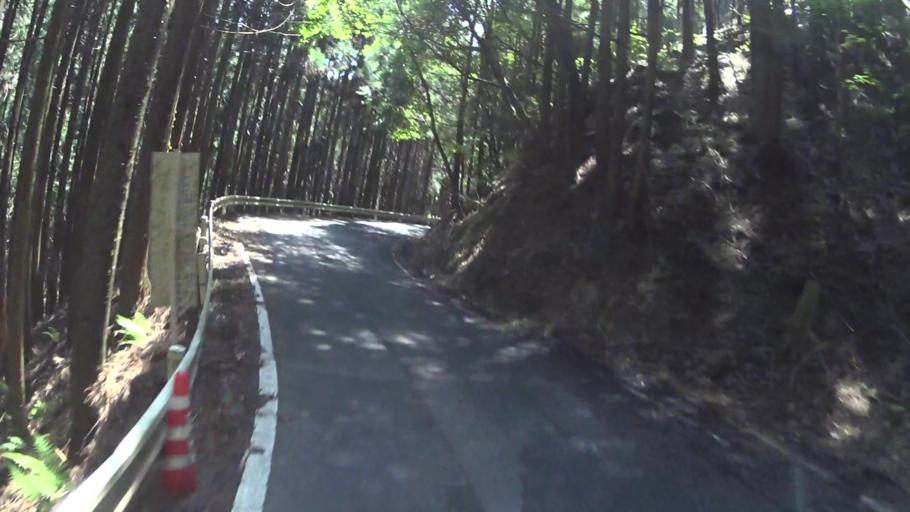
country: JP
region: Kyoto
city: Kameoka
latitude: 35.1176
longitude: 135.5866
